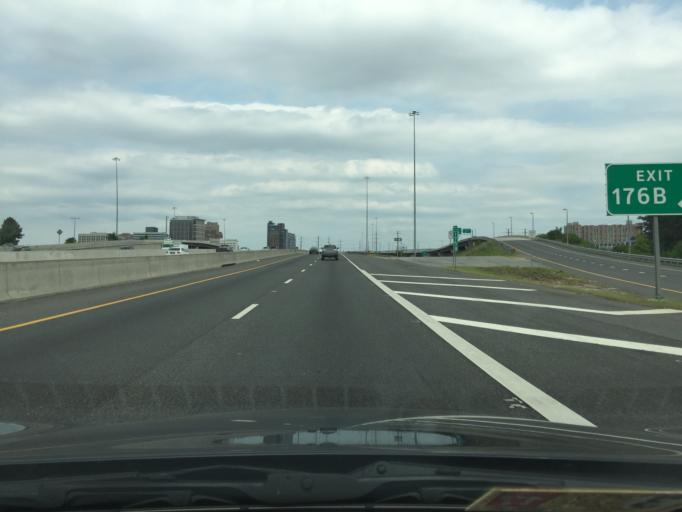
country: US
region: Virginia
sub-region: Fairfax County
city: Huntington
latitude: 38.8007
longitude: -77.0823
